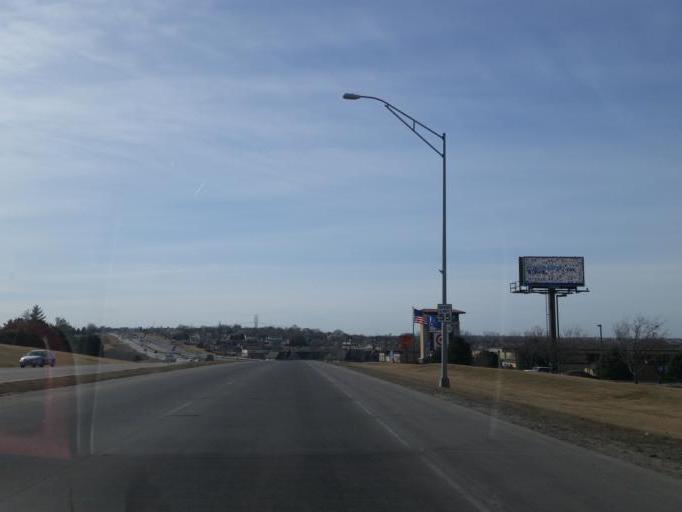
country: US
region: Nebraska
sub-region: Sarpy County
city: Offutt Air Force Base
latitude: 41.1396
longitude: -95.9679
